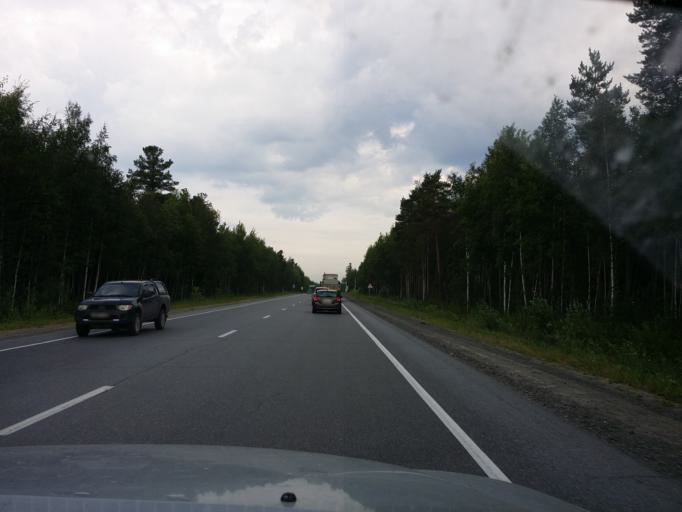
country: RU
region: Khanty-Mansiyskiy Avtonomnyy Okrug
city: Megion
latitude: 61.0565
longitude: 76.3012
